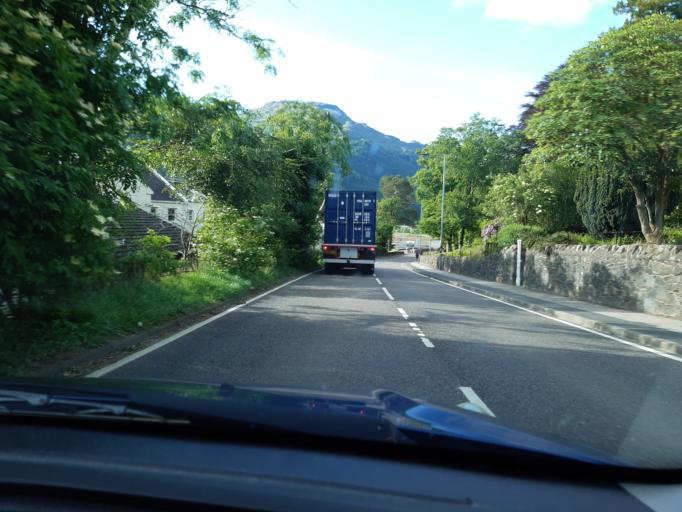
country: GB
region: Scotland
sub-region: Argyll and Bute
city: Garelochhead
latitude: 56.1992
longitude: -4.7454
